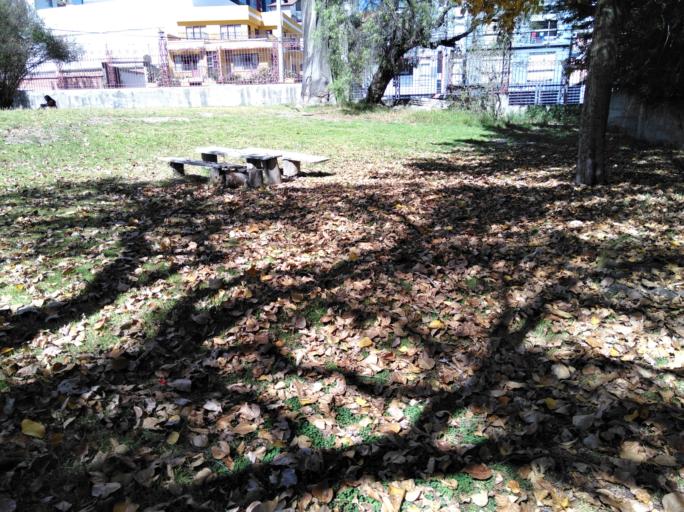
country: BO
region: La Paz
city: La Paz
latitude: -16.5393
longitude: -68.0692
